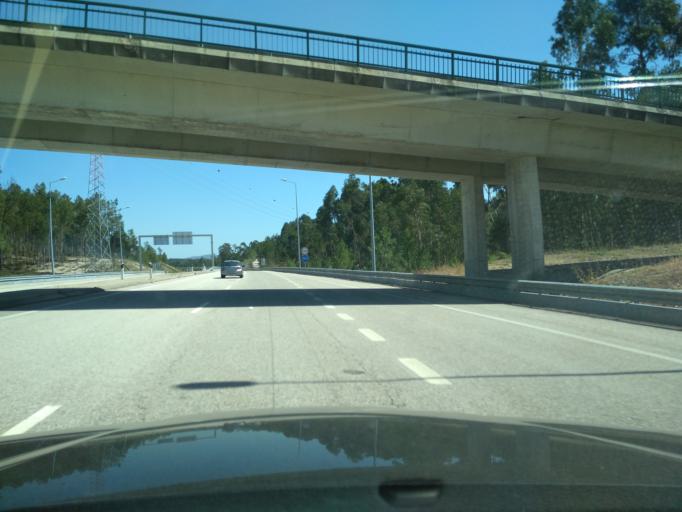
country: PT
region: Leiria
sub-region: Pombal
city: Lourical
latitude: 39.9830
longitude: -8.7274
